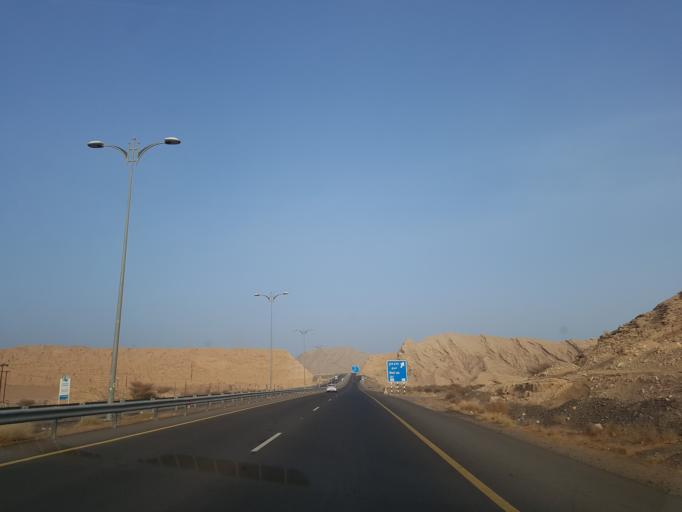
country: OM
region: Al Buraimi
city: Al Buraymi
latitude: 24.2336
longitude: 55.9418
